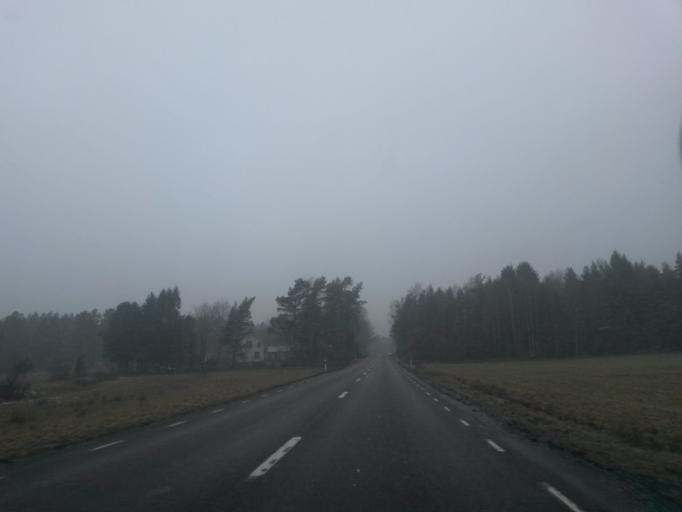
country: SE
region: Vaestra Goetaland
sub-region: Vanersborgs Kommun
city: Vargon
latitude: 58.2304
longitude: 12.4223
